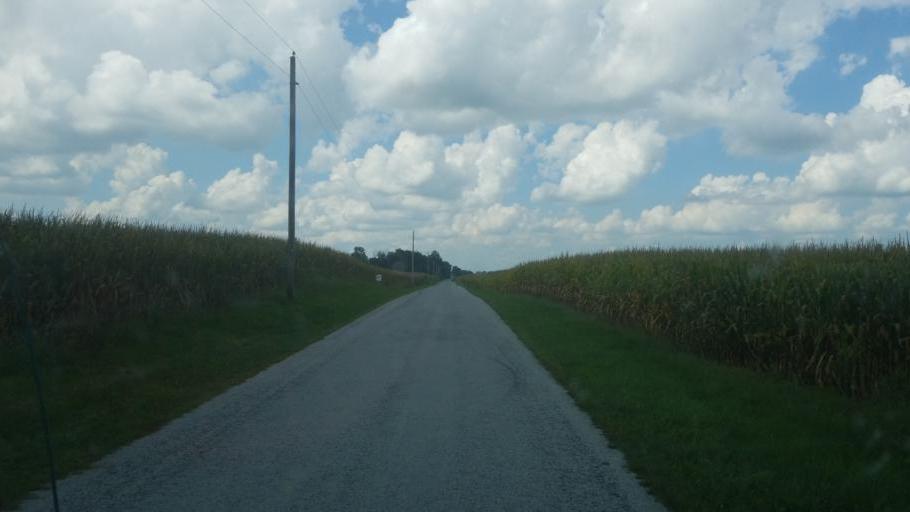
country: US
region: Ohio
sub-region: Hardin County
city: Kenton
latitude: 40.6881
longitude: -83.5672
